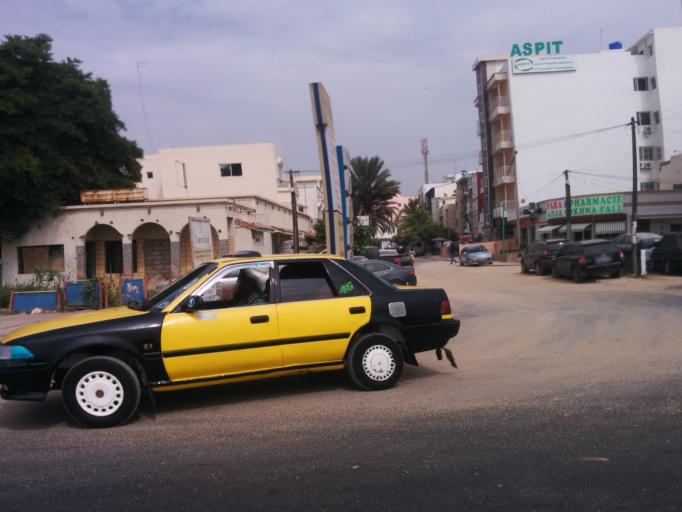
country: SN
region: Dakar
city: Mermoz Boabab
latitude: 14.7290
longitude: -17.4723
